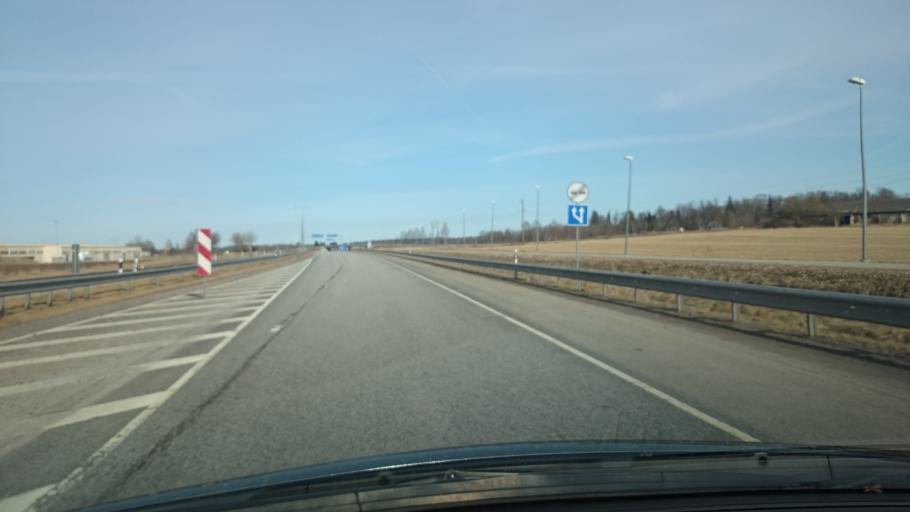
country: EE
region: Jaervamaa
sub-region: Paide linn
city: Paide
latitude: 58.9129
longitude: 25.6008
